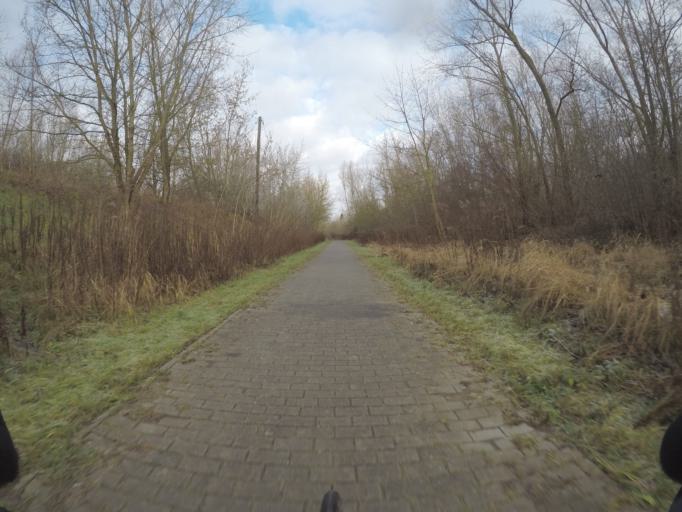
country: DE
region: Berlin
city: Stadtrandsiedlung Malchow
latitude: 52.5789
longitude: 13.4937
